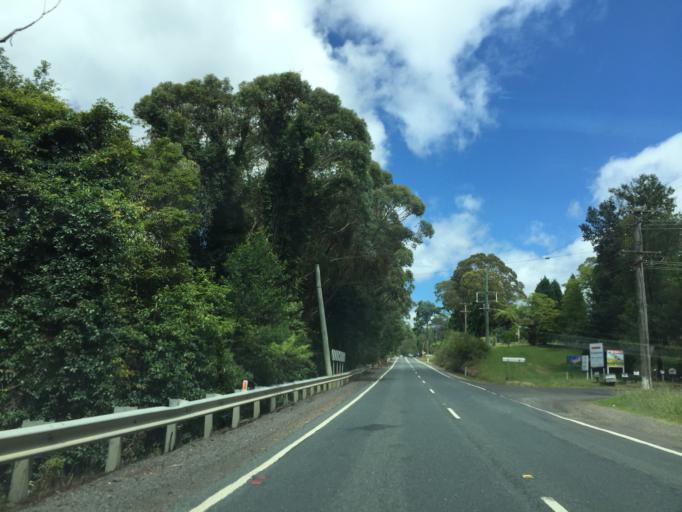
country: AU
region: New South Wales
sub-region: Blue Mountains Municipality
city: Hazelbrook
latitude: -33.5064
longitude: 150.5017
